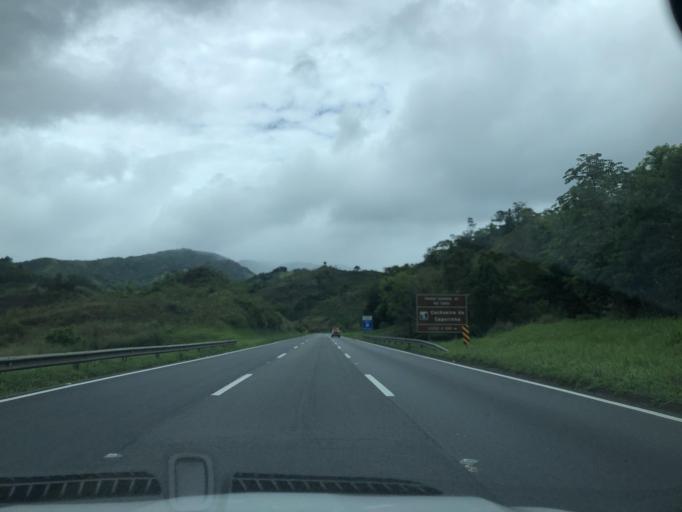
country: BR
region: Sao Paulo
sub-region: Cajati
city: Cajati
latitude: -24.8292
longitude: -48.2194
